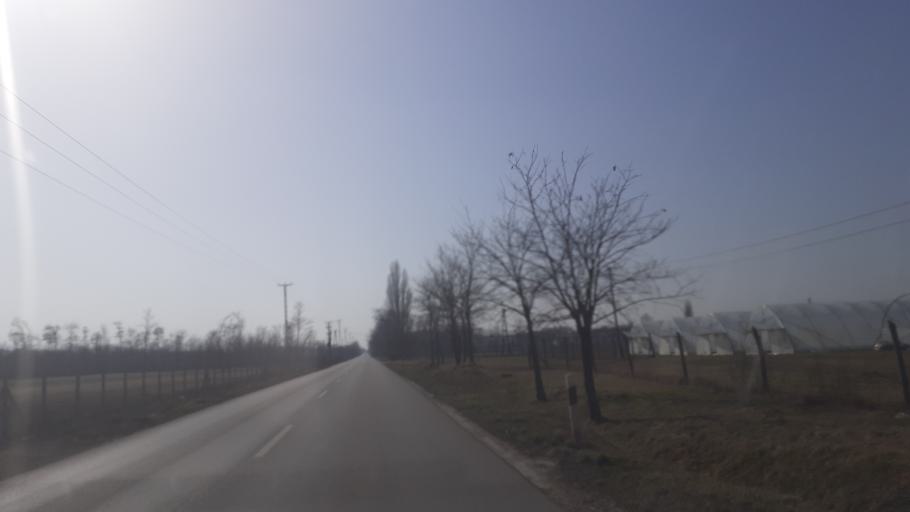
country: HU
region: Bacs-Kiskun
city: Lajosmizse
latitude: 47.0210
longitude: 19.5239
